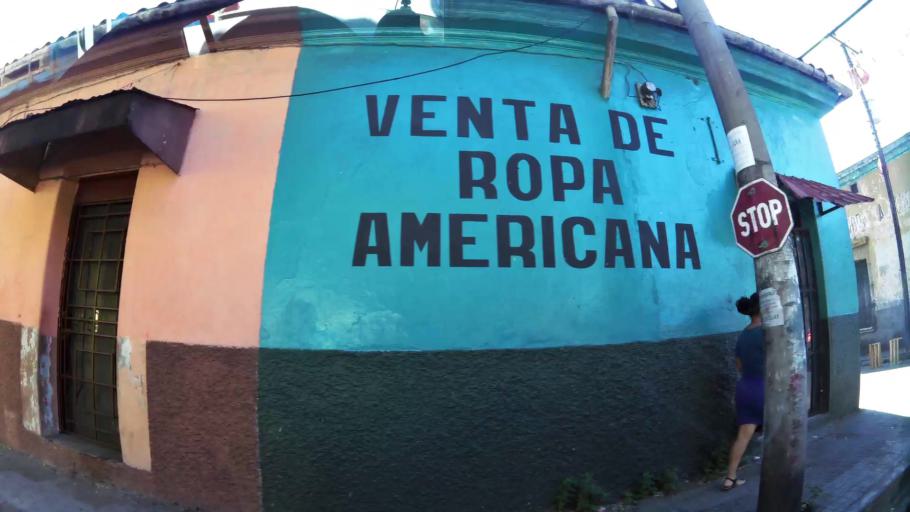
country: SV
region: Santa Ana
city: Santa Ana
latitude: 13.9947
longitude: -89.5611
